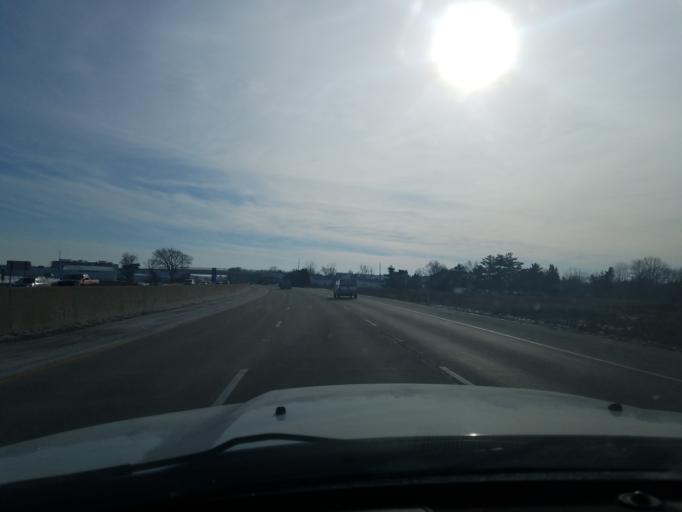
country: US
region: Indiana
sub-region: Allen County
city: Fort Wayne
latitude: 41.0484
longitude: -85.2522
